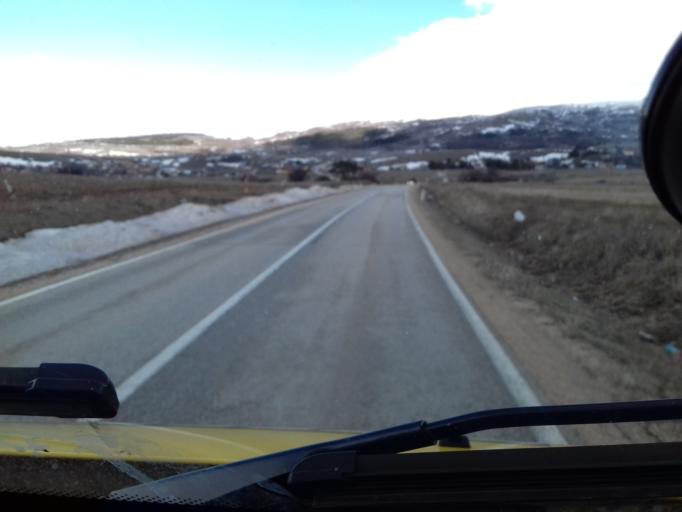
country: BA
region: Federation of Bosnia and Herzegovina
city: Tomislavgrad
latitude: 43.7518
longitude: 17.2304
